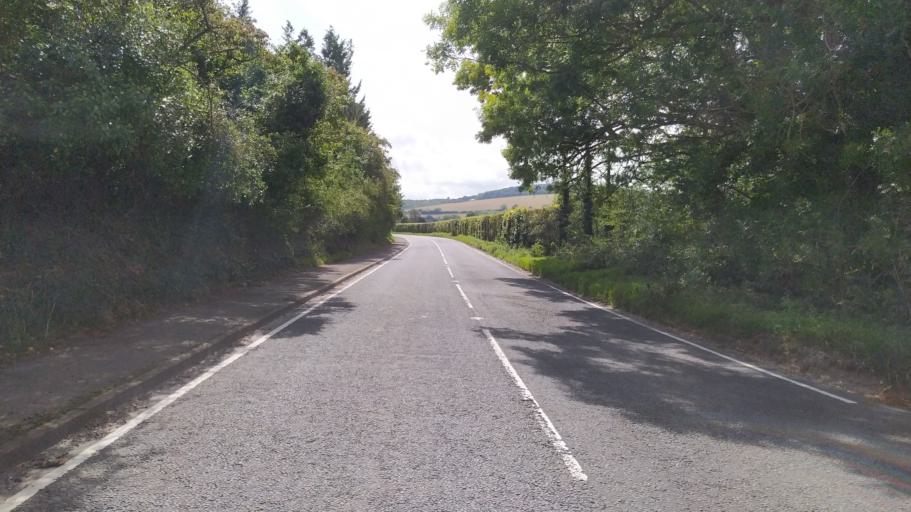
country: GB
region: England
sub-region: Dorset
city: Blandford Forum
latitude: 50.8903
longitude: -2.1952
